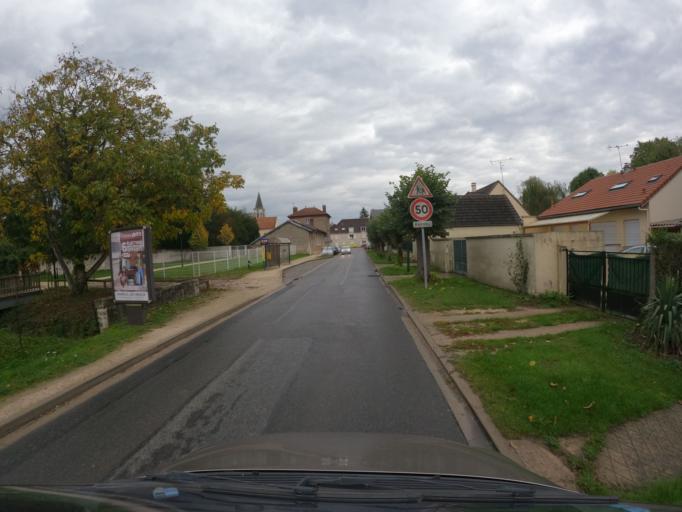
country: FR
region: Ile-de-France
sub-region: Departement de Seine-et-Marne
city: Serris
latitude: 48.8165
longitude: 2.7923
